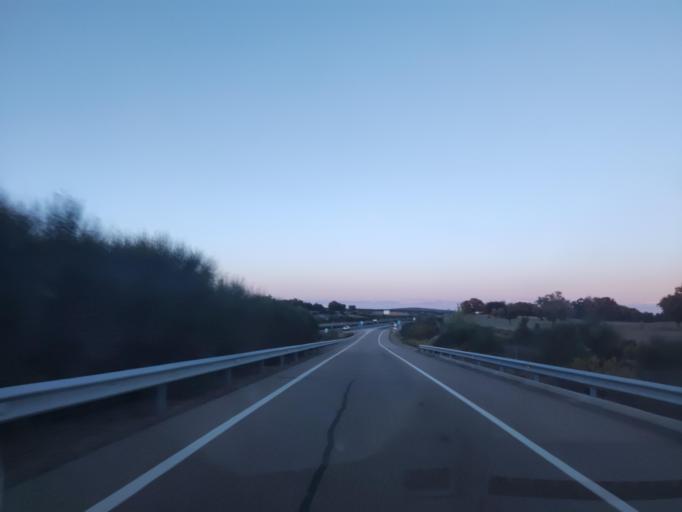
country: ES
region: Castille and Leon
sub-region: Provincia de Salamanca
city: San Munoz
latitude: 40.8207
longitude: -6.1174
